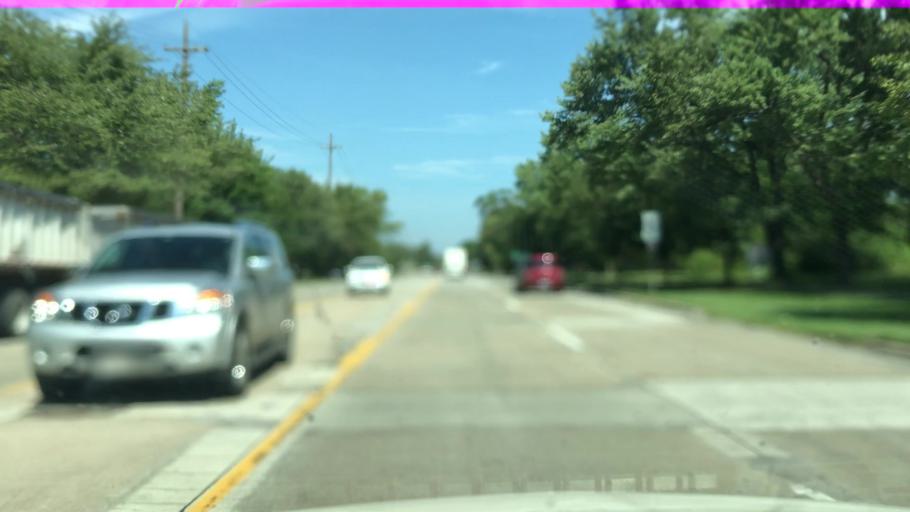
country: US
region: Michigan
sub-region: Wayne County
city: Wayne
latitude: 42.2500
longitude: -83.3477
